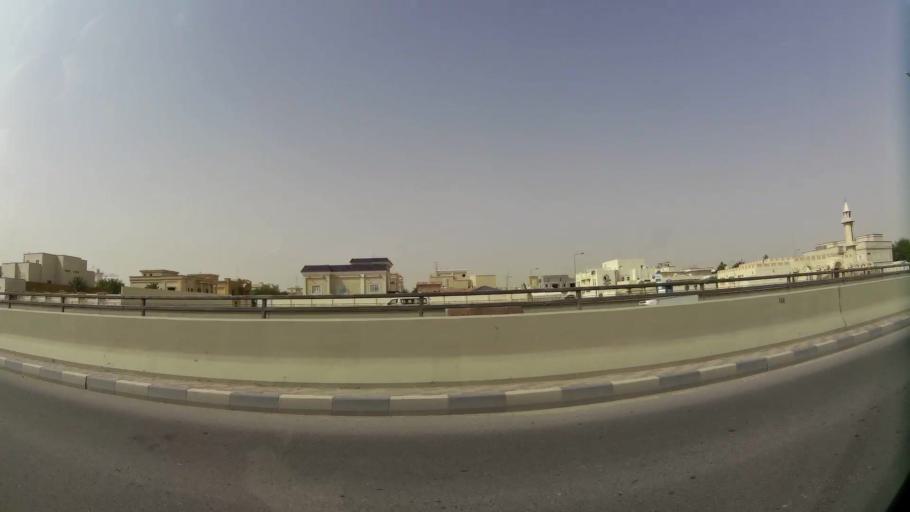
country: QA
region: Baladiyat ad Dawhah
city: Doha
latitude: 25.2781
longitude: 51.4877
